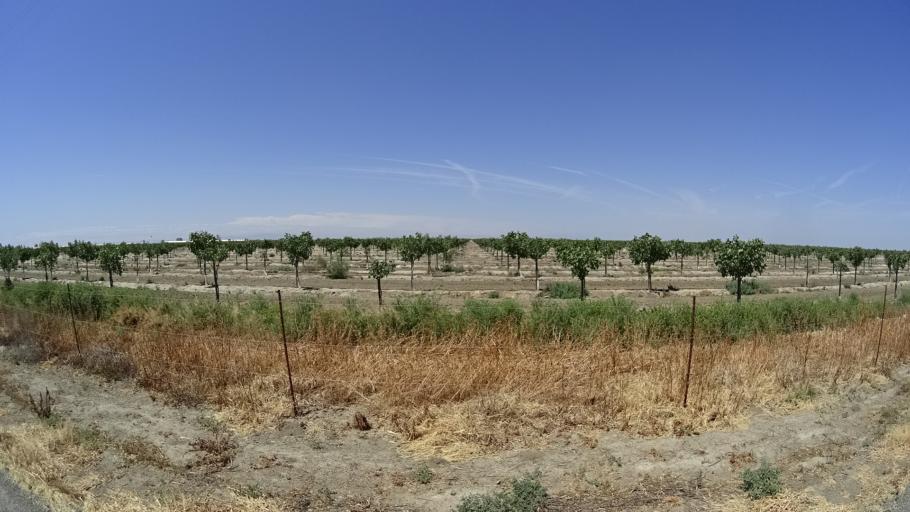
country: US
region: California
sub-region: Kings County
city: Stratford
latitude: 36.1952
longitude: -119.7086
